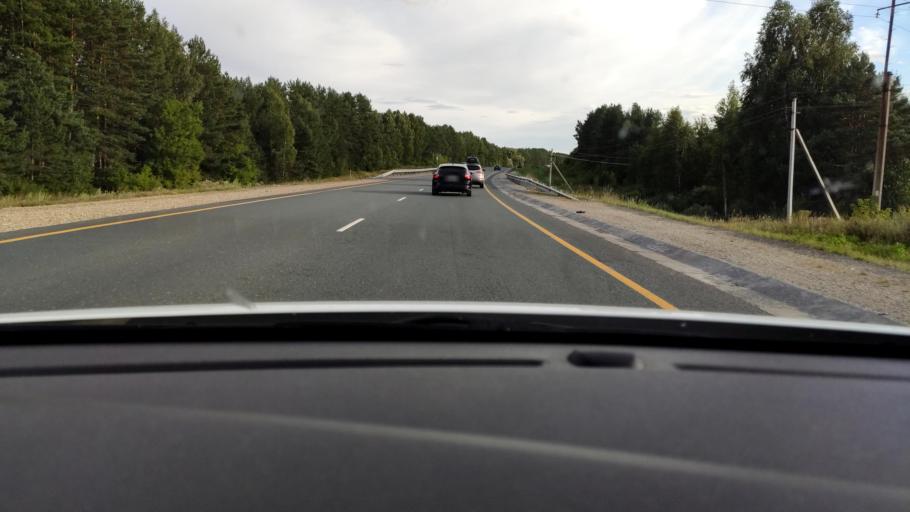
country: RU
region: Mariy-El
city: Pomary
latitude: 55.9983
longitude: 48.3823
